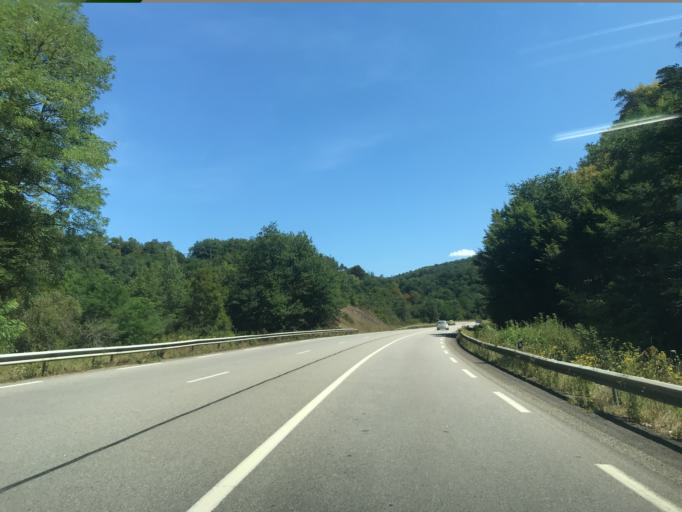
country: FR
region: Limousin
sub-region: Departement de la Correze
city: Laguenne
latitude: 45.2573
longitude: 1.7795
